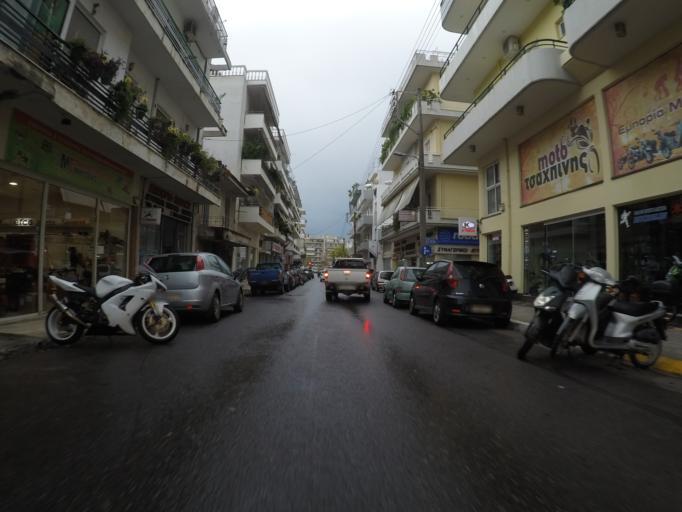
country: GR
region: Peloponnese
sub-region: Nomos Messinias
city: Kalamata
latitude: 37.0410
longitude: 22.1069
